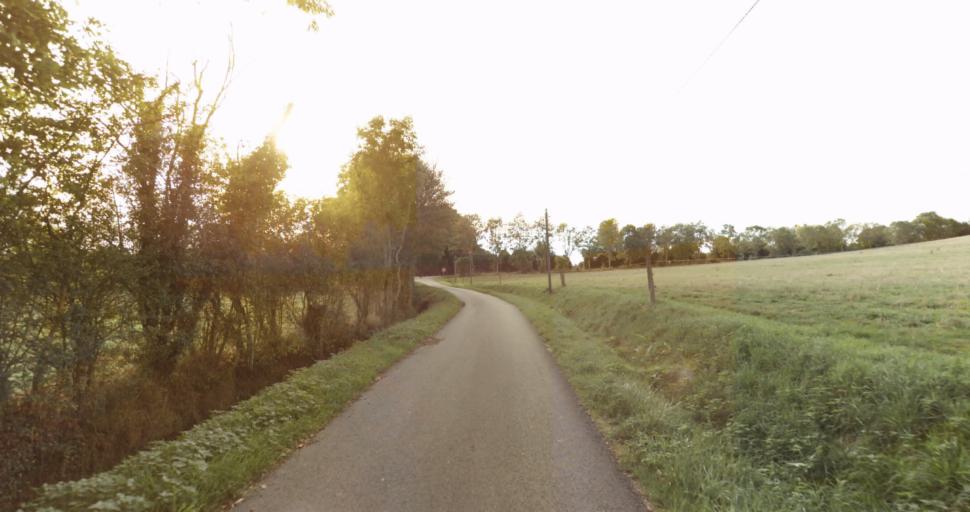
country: FR
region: Lower Normandy
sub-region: Departement de l'Orne
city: Gace
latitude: 48.7199
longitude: 0.2819
